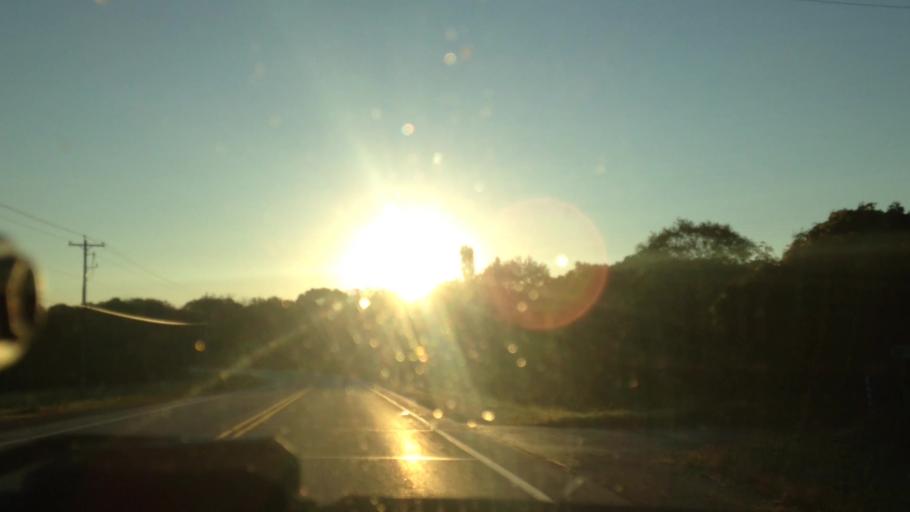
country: US
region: Wisconsin
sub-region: Washington County
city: Newburg
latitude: 43.4229
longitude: -88.0661
